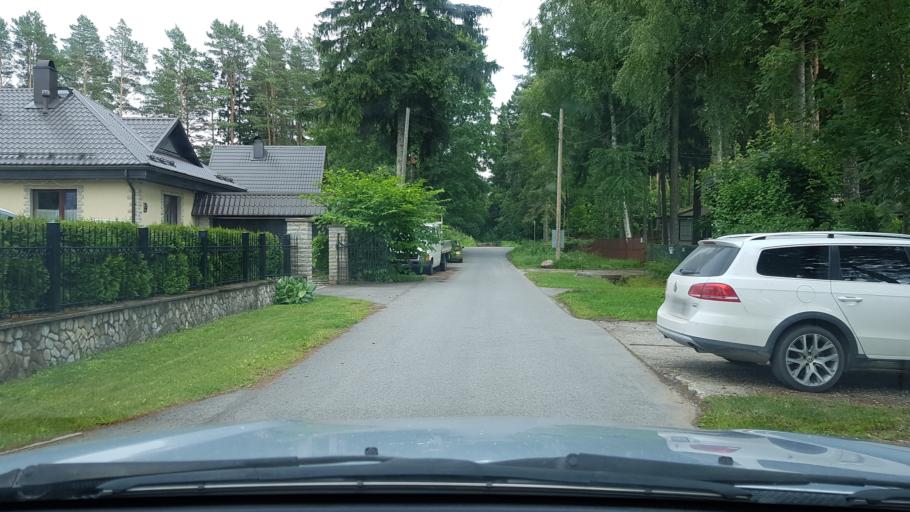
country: EE
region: Ida-Virumaa
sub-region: Narva-Joesuu linn
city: Narva-Joesuu
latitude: 59.4495
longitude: 28.0282
